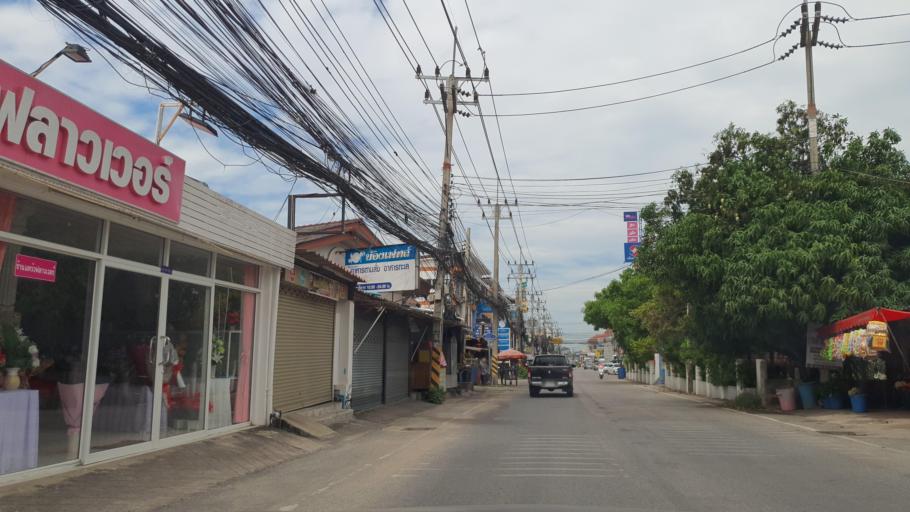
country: TH
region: Chon Buri
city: Bang Lamung
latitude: 12.9829
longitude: 100.9342
